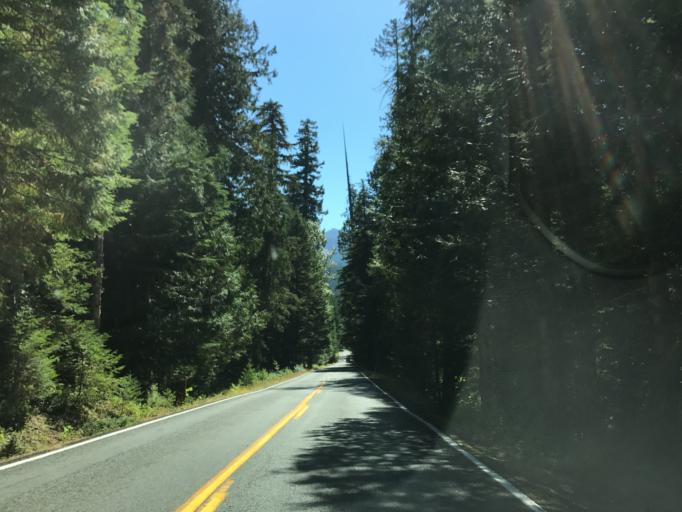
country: US
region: Washington
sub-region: Pierce County
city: Buckley
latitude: 46.7780
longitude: -121.5513
